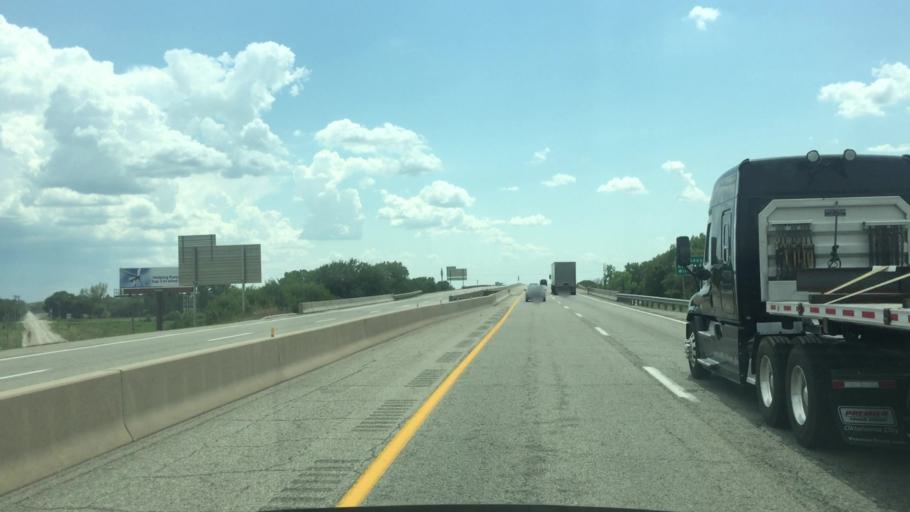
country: US
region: Kansas
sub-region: Lyon County
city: Emporia
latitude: 38.4056
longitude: -96.2443
